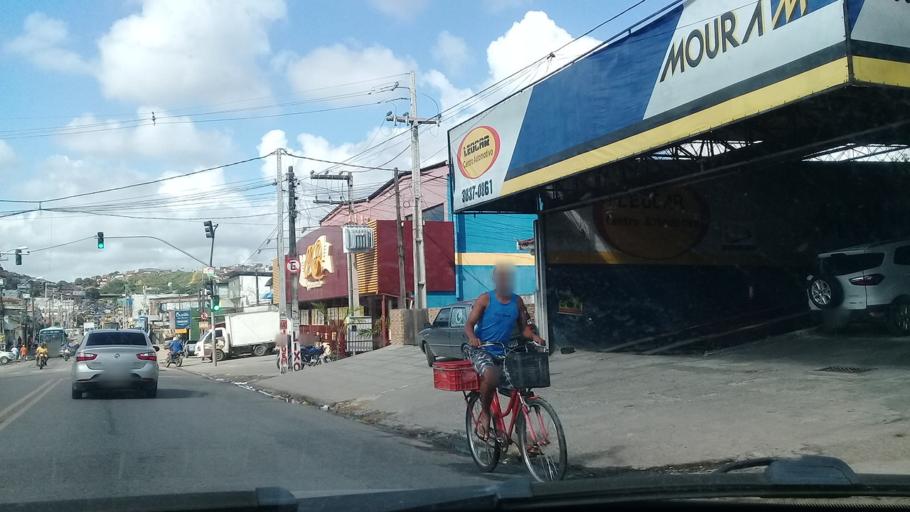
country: BR
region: Pernambuco
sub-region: Jaboatao Dos Guararapes
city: Jaboatao dos Guararapes
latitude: -8.1133
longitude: -34.9388
